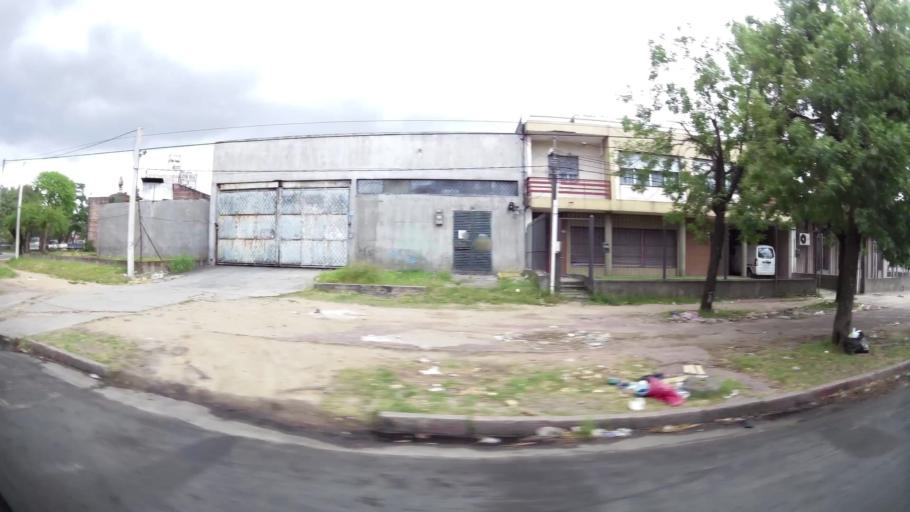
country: UY
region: Montevideo
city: Montevideo
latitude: -34.8737
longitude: -56.1525
